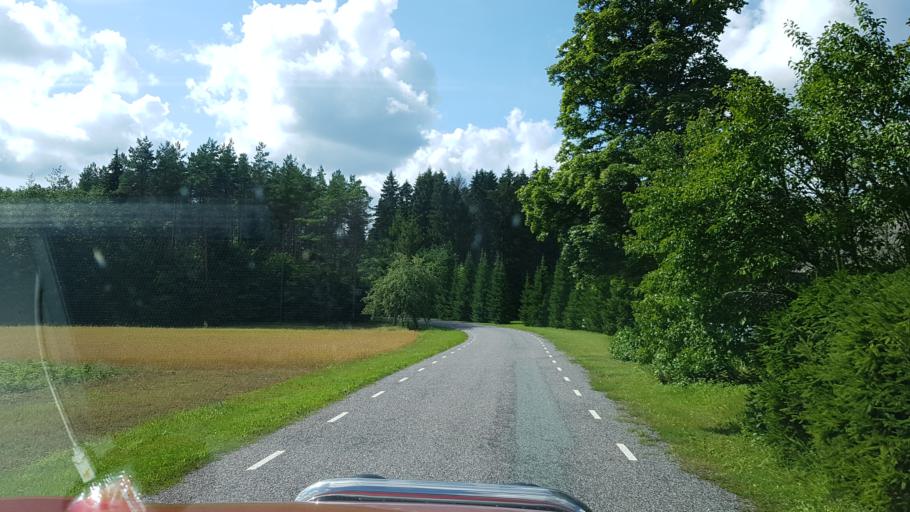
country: EE
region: Raplamaa
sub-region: Maerjamaa vald
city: Marjamaa
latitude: 58.9619
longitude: 24.6050
